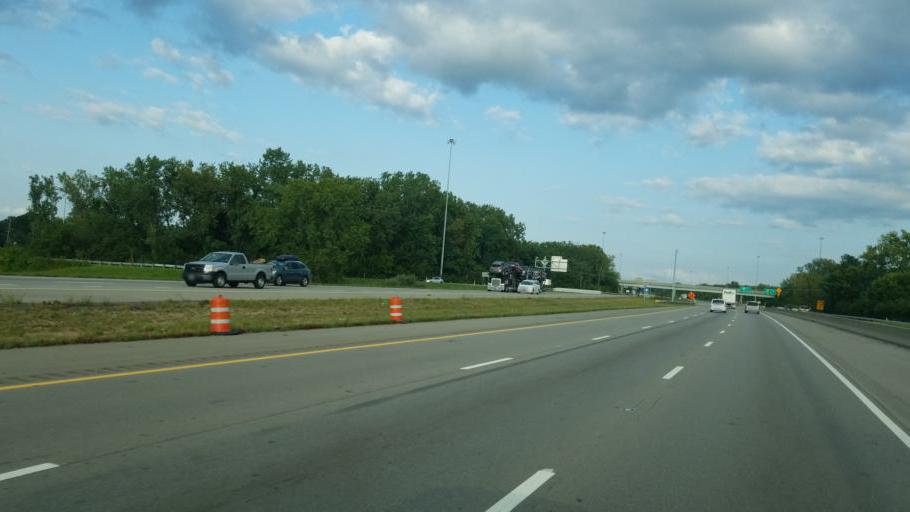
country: US
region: Ohio
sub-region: Franklin County
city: Obetz
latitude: 39.8755
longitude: -83.0065
